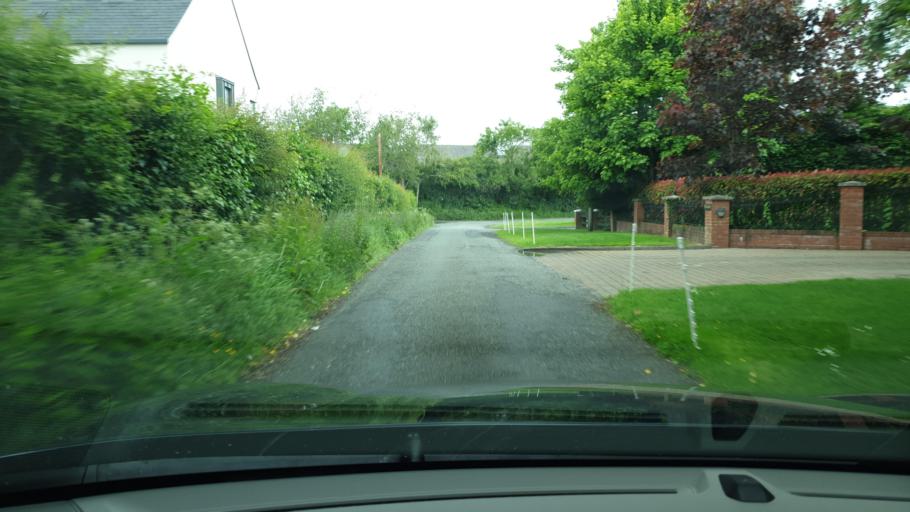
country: IE
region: Leinster
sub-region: An Mhi
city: Ashbourne
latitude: 53.4990
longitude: -6.3903
